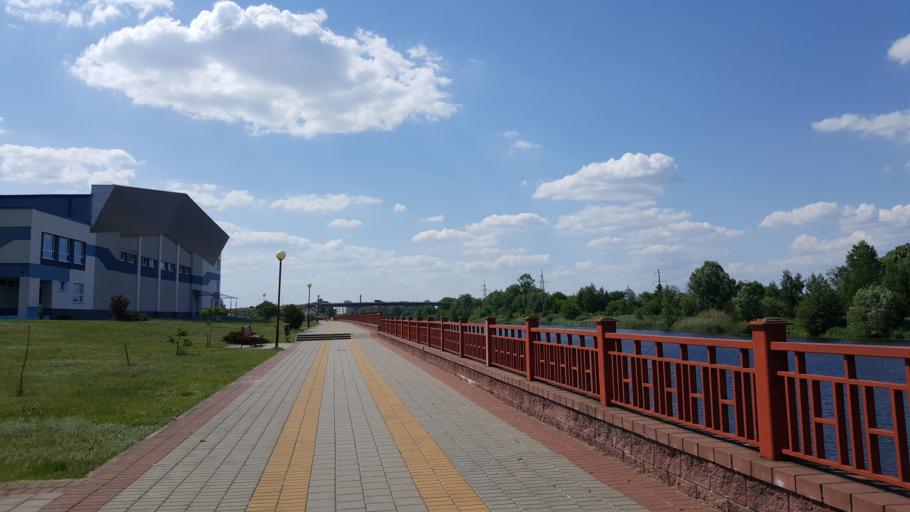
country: BY
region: Brest
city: Horad Kobryn
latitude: 52.2139
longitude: 24.3657
